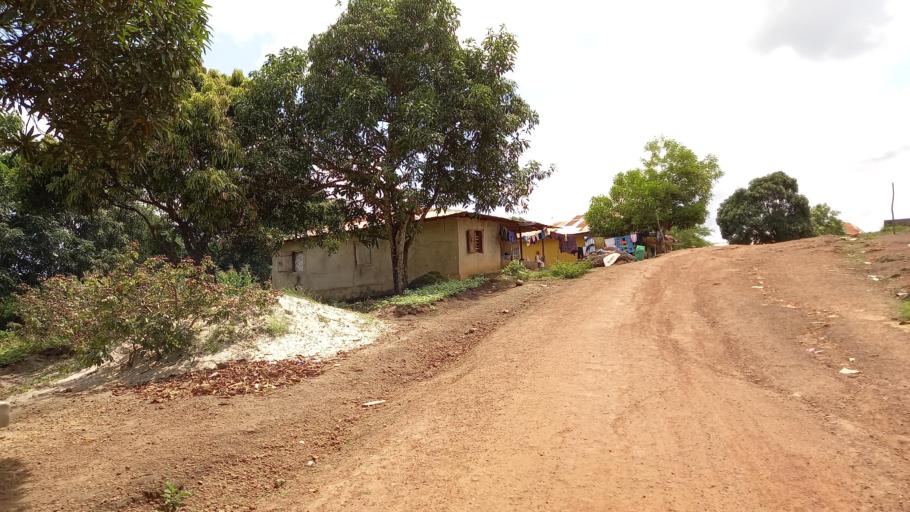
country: SL
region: Northern Province
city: Kamakwie
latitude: 9.5013
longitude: -12.2436
